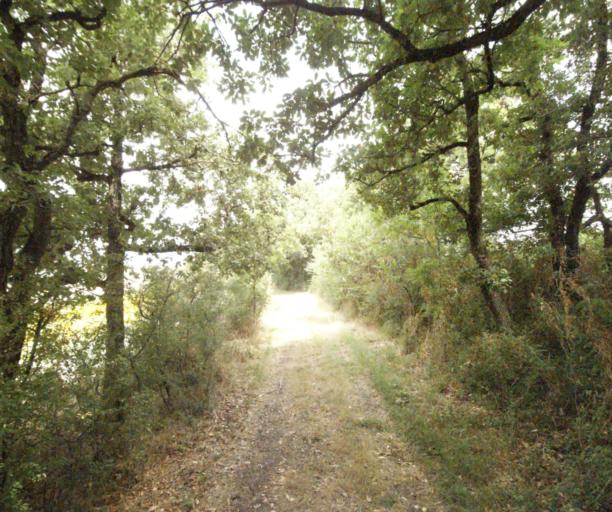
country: FR
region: Midi-Pyrenees
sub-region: Departement de la Haute-Garonne
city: Saint-Felix-Lauragais
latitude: 43.4251
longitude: 1.9283
